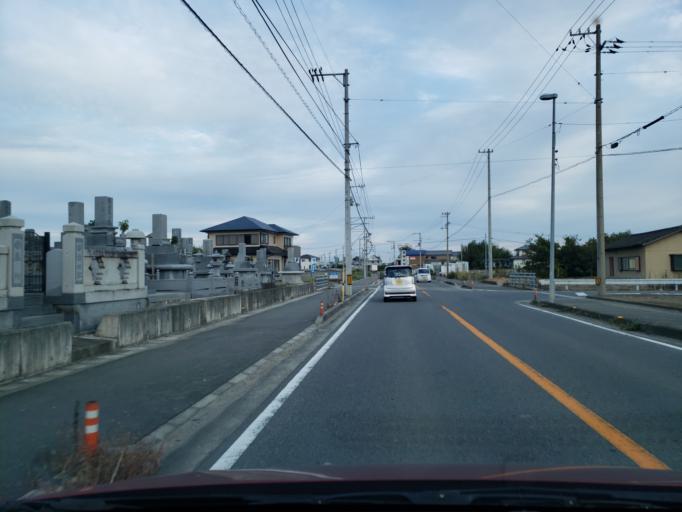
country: JP
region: Tokushima
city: Kamojimacho-jogejima
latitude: 34.0999
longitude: 134.3330
